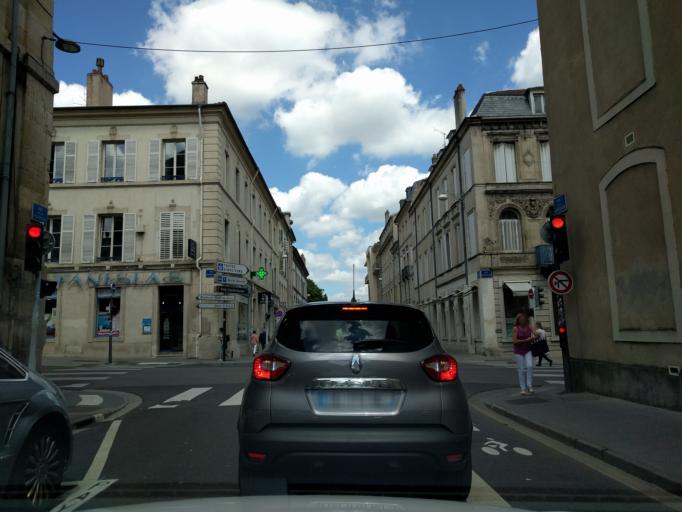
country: FR
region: Lorraine
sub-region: Departement de Meurthe-et-Moselle
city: Nancy
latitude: 48.6921
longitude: 6.1792
